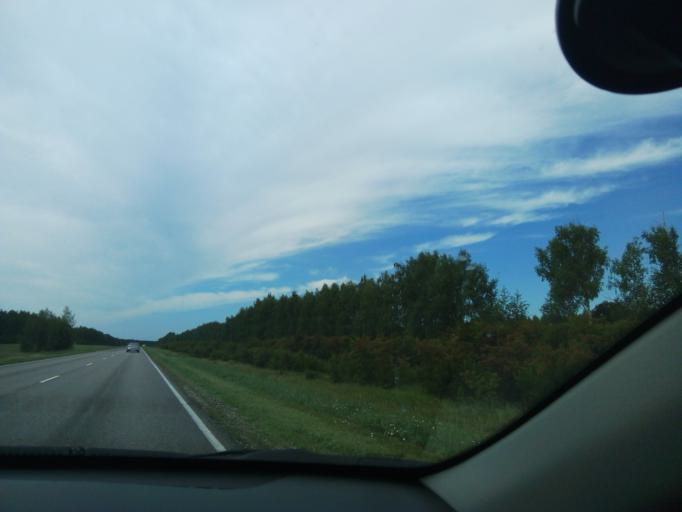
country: RU
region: Tambov
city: Zavoronezhskoye
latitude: 52.6128
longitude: 40.7820
